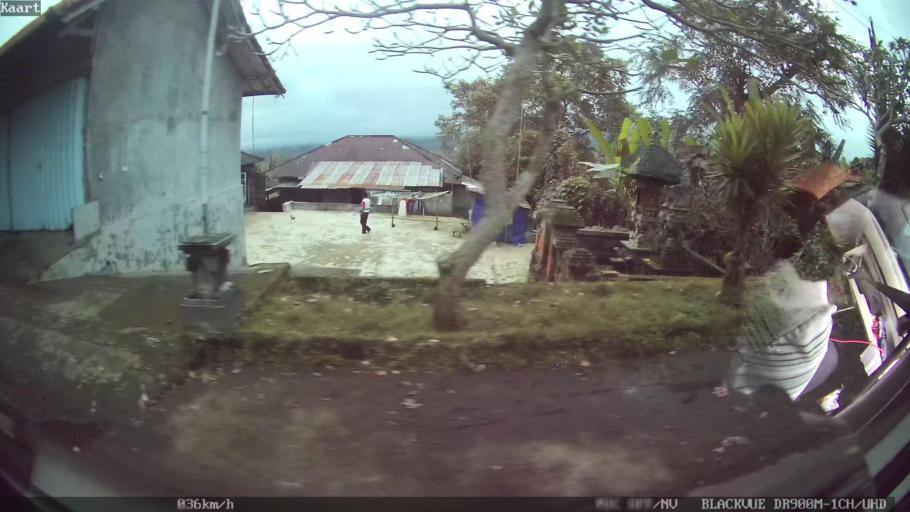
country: ID
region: Bali
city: Peneng
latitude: -8.3512
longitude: 115.2073
